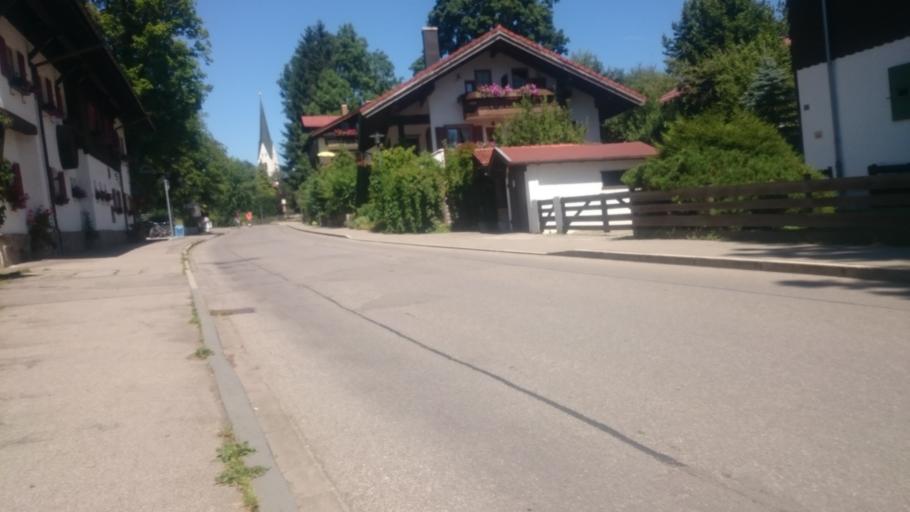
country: DE
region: Bavaria
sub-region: Swabia
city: Oberstdorf
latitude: 47.4041
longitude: 10.2780
